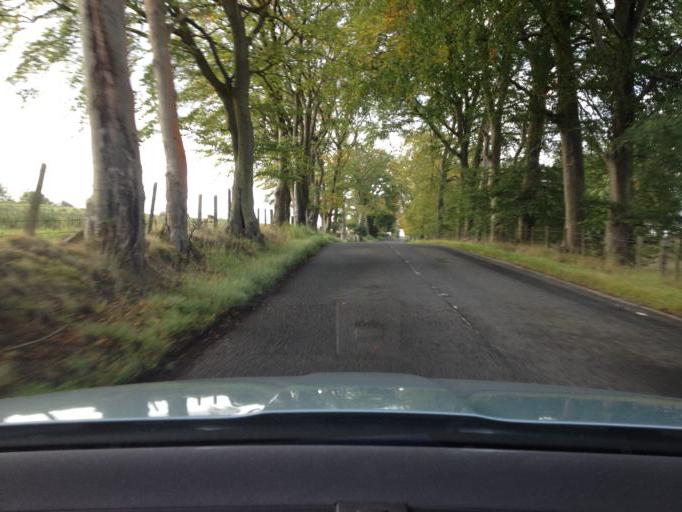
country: GB
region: Scotland
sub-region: West Lothian
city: West Calder
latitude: 55.8349
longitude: -3.5354
